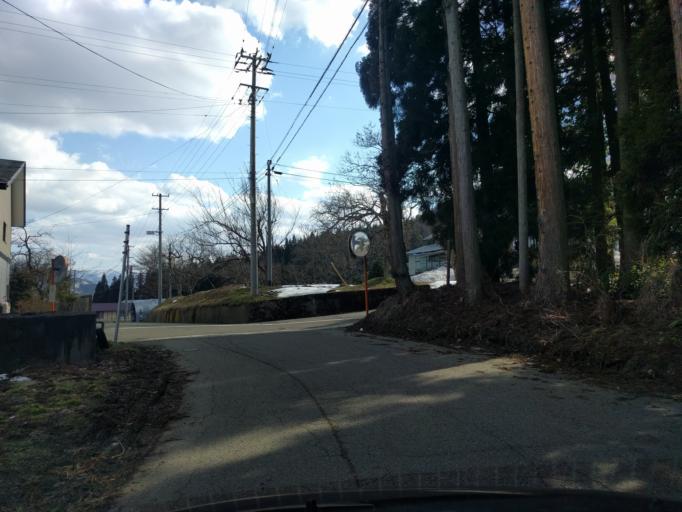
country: JP
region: Fukushima
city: Kitakata
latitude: 37.4511
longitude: 139.7992
